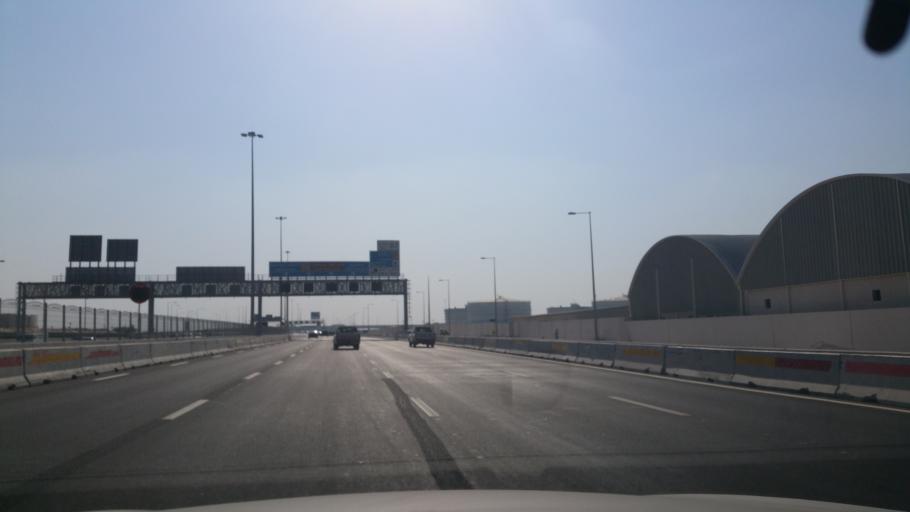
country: QA
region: Baladiyat ad Dawhah
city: Doha
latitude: 25.2334
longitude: 51.5183
